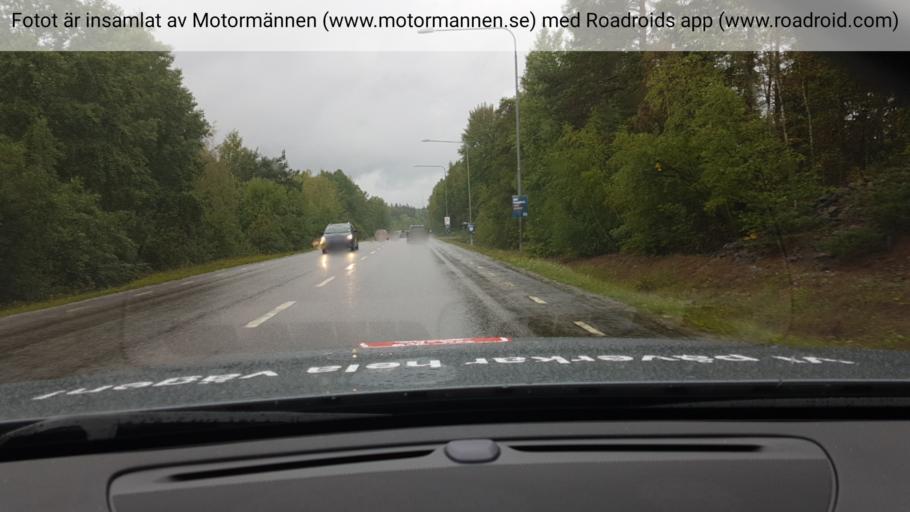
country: SE
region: Stockholm
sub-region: Haninge Kommun
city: Handen
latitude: 59.1974
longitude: 18.1225
